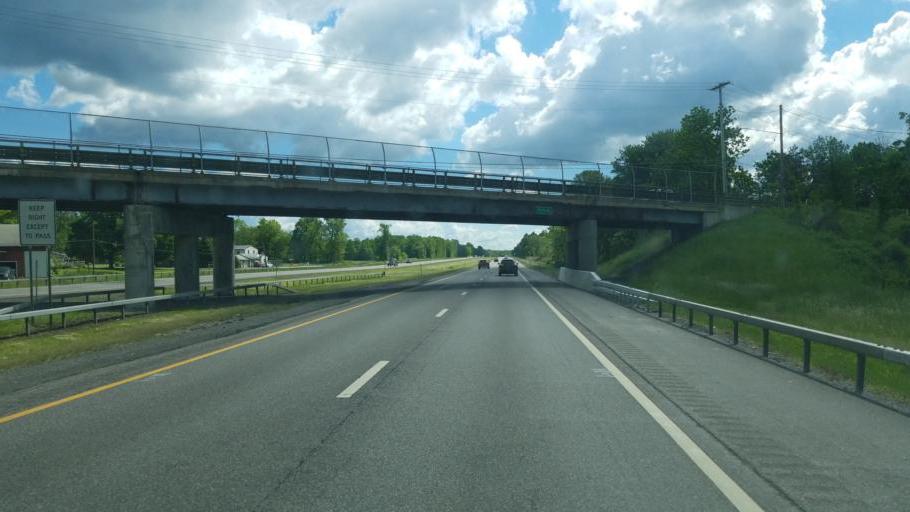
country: US
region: New York
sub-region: Madison County
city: Bolivar
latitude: 43.0917
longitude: -75.9016
